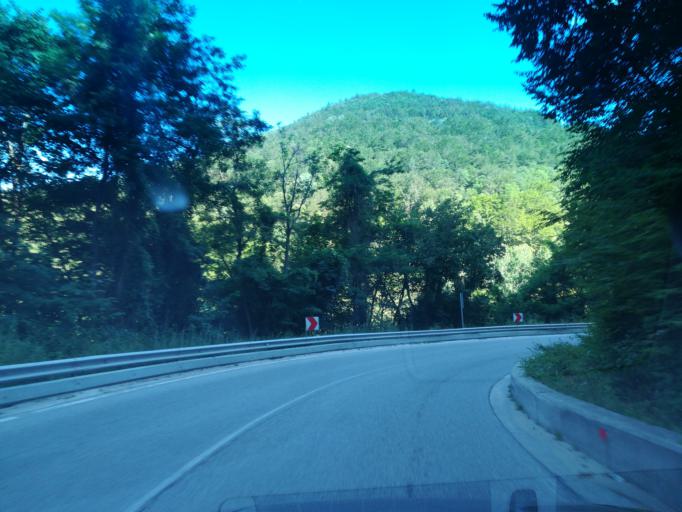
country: BG
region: Smolyan
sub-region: Obshtina Chepelare
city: Chepelare
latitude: 41.8039
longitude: 24.7103
